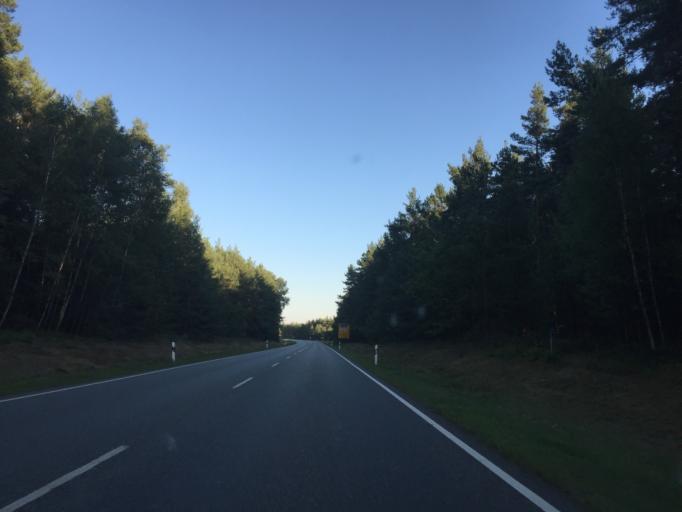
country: DE
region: Bavaria
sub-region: Upper Palatinate
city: Schwarzenbach
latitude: 49.7280
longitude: 11.9635
